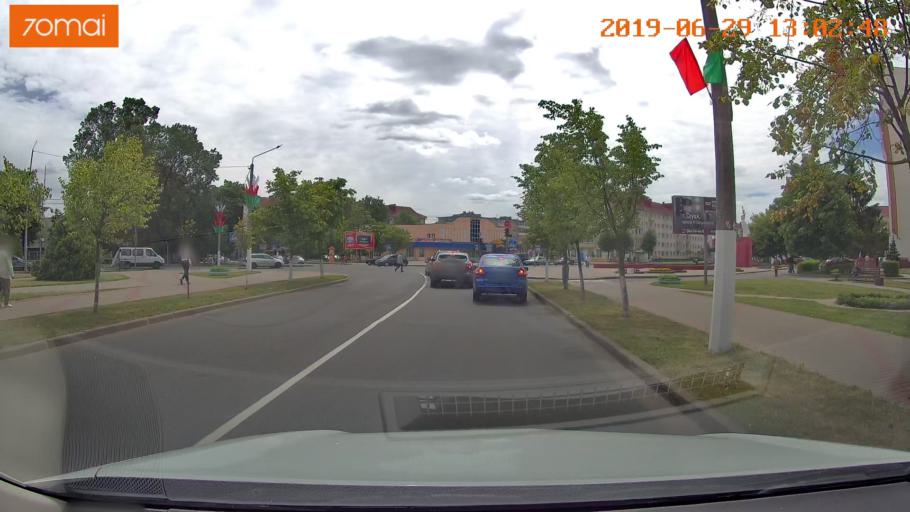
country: BY
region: Minsk
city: Slutsk
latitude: 53.0333
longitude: 27.5601
